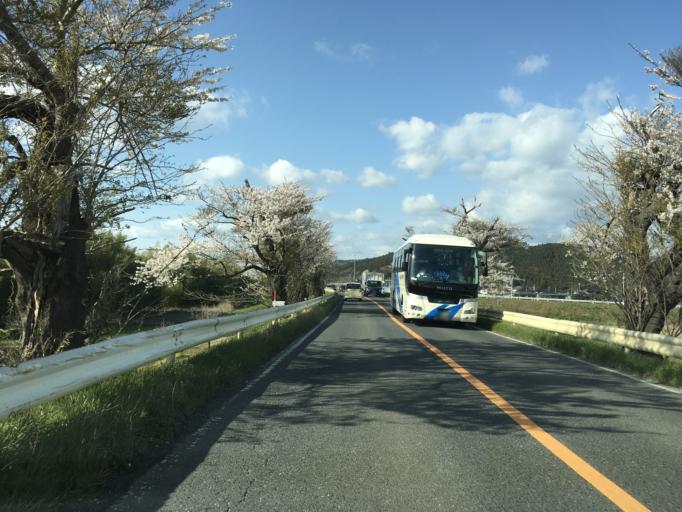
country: JP
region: Miyagi
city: Wakuya
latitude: 38.6471
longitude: 141.2865
